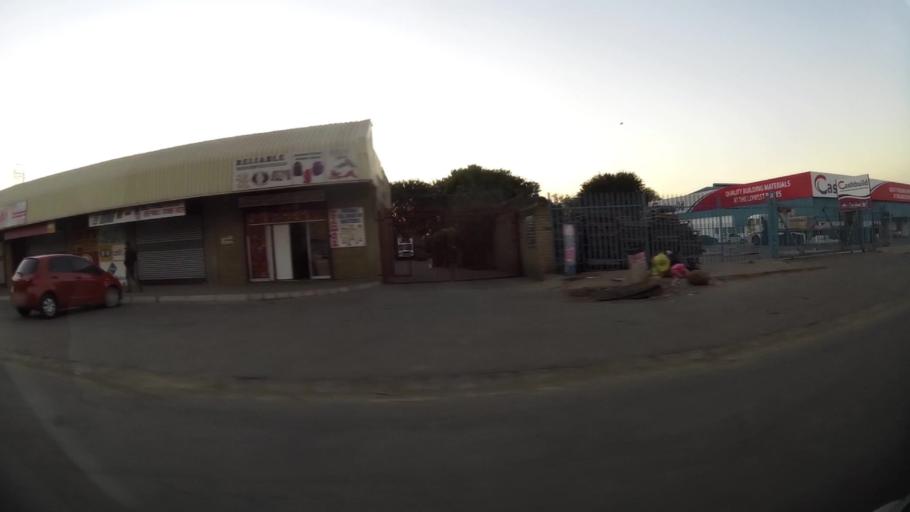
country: ZA
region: North-West
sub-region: Bojanala Platinum District Municipality
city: Rustenburg
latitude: -25.6664
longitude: 27.2381
